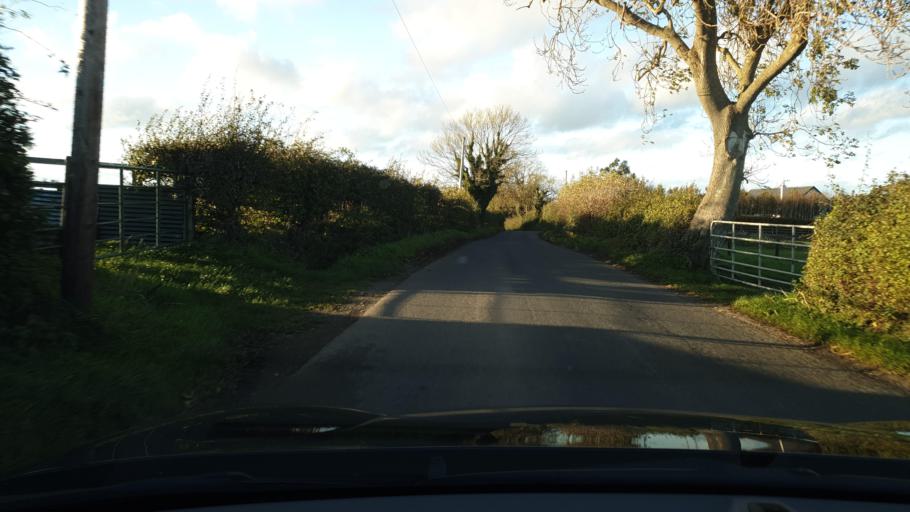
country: IE
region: Leinster
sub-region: An Mhi
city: Stamullin
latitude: 53.6187
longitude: -6.2576
